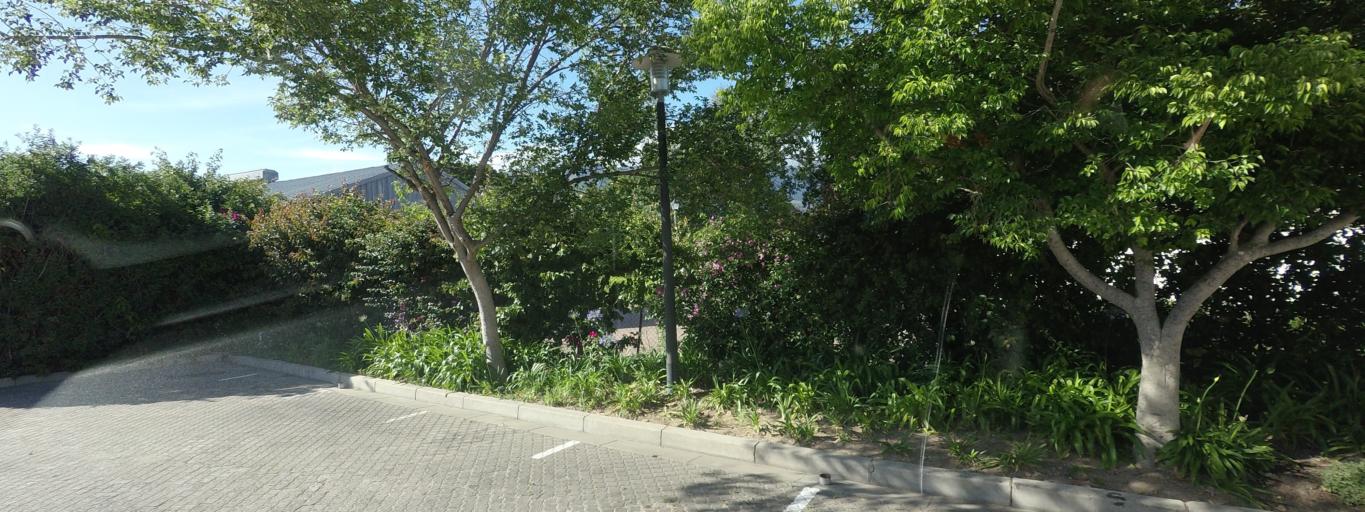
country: ZA
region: Western Cape
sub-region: Cape Winelands District Municipality
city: Paarl
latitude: -33.9069
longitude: 19.1145
